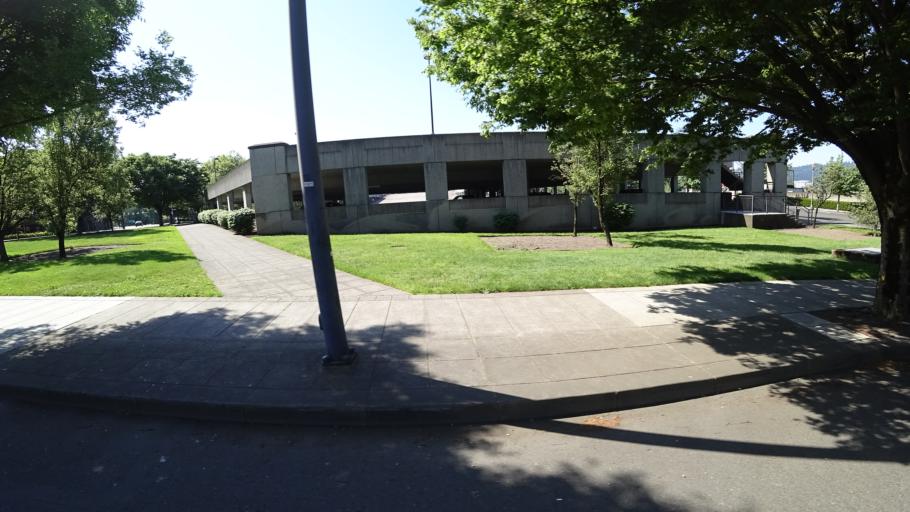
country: US
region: Oregon
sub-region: Multnomah County
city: Portland
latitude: 45.5343
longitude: -122.6684
